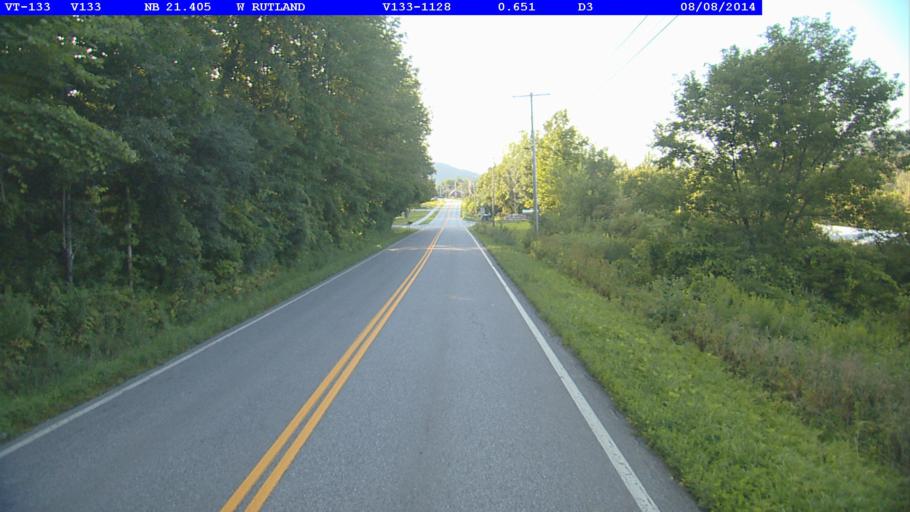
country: US
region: Vermont
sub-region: Rutland County
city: West Rutland
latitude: 43.5790
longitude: -73.0389
